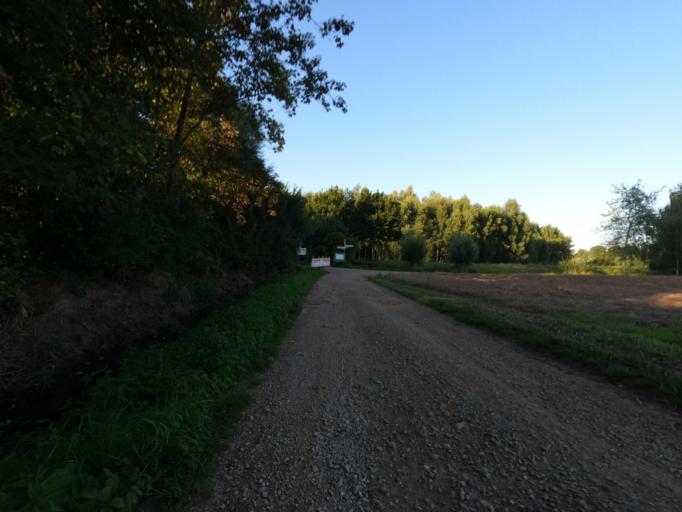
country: DE
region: North Rhine-Westphalia
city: Julich
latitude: 50.9427
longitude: 6.3251
